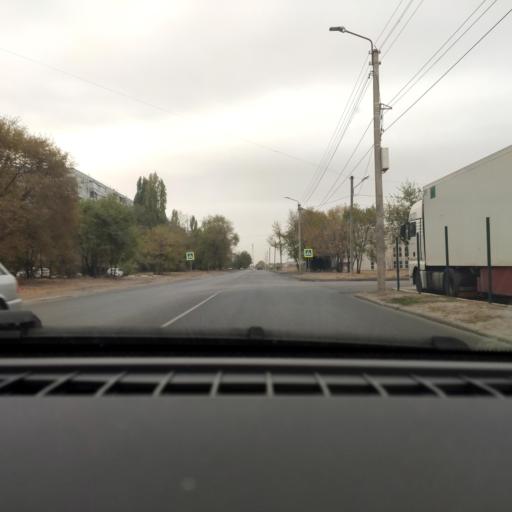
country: RU
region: Voronezj
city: Maslovka
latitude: 51.5984
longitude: 39.2368
